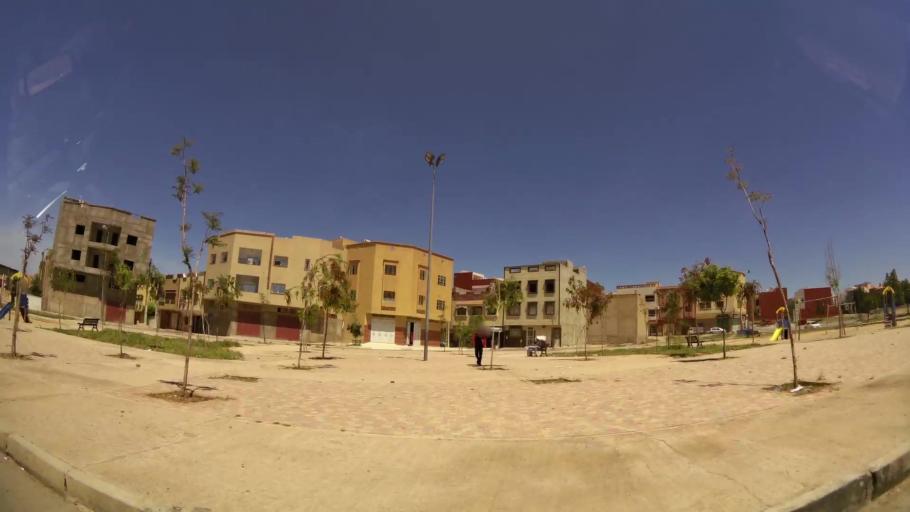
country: MA
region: Oriental
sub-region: Oujda-Angad
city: Oujda
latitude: 34.6558
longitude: -1.9204
